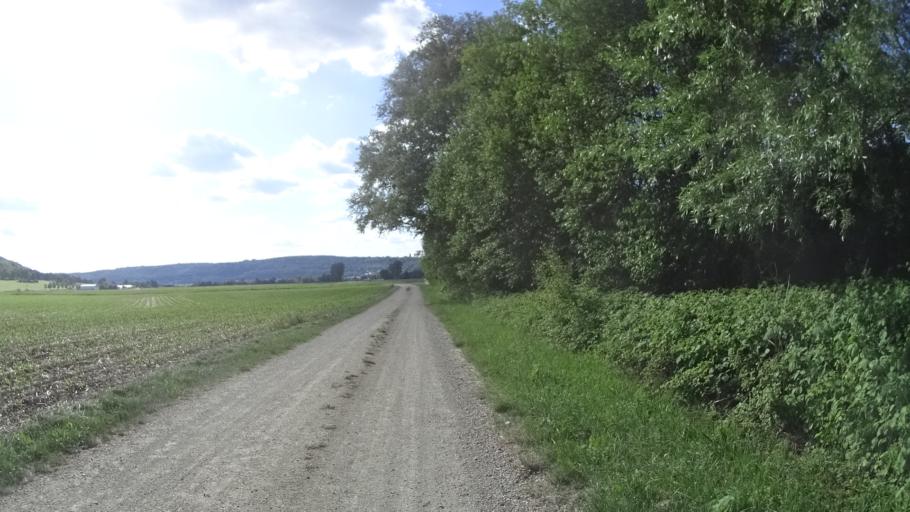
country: DE
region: Bavaria
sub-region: Upper Palatinate
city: Dietfurt
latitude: 49.0207
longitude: 11.4969
